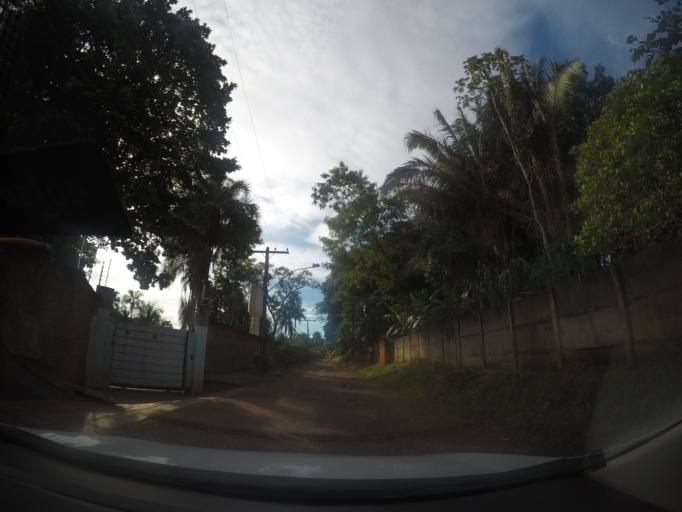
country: BR
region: Goias
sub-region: Goiania
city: Goiania
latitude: -16.6417
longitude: -49.3496
